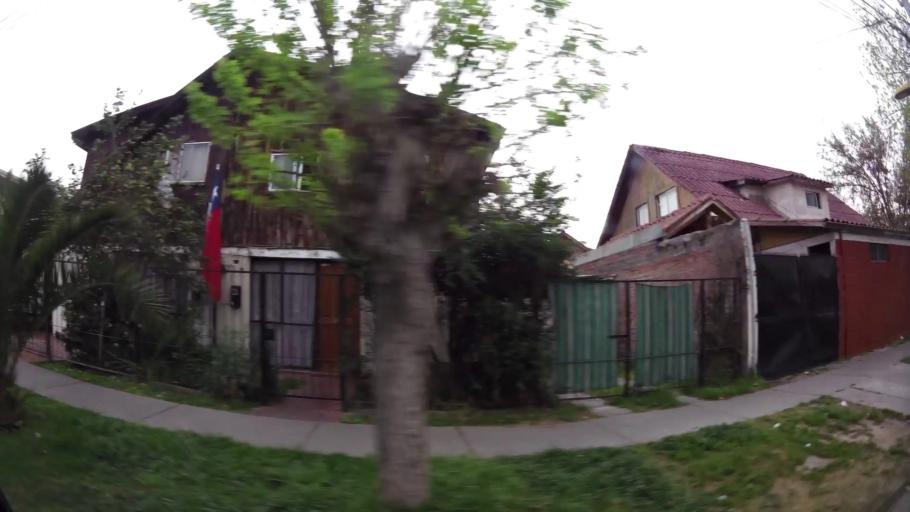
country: CL
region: Santiago Metropolitan
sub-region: Provincia de Santiago
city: Lo Prado
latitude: -33.5252
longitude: -70.7705
